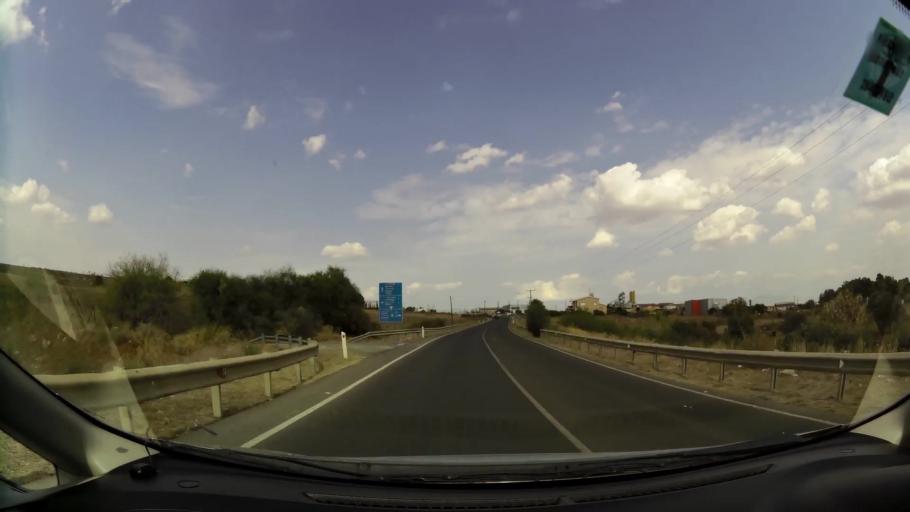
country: CY
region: Lefkosia
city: Tseri
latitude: 35.0936
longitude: 33.3269
